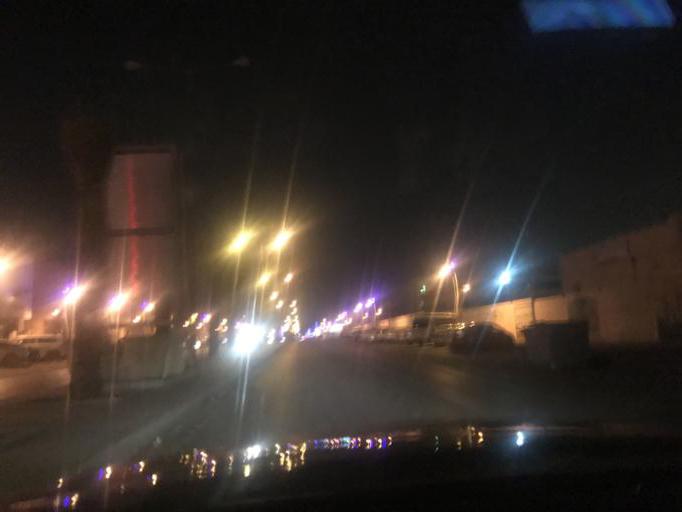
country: SA
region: Ar Riyad
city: Riyadh
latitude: 24.7614
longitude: 46.7985
